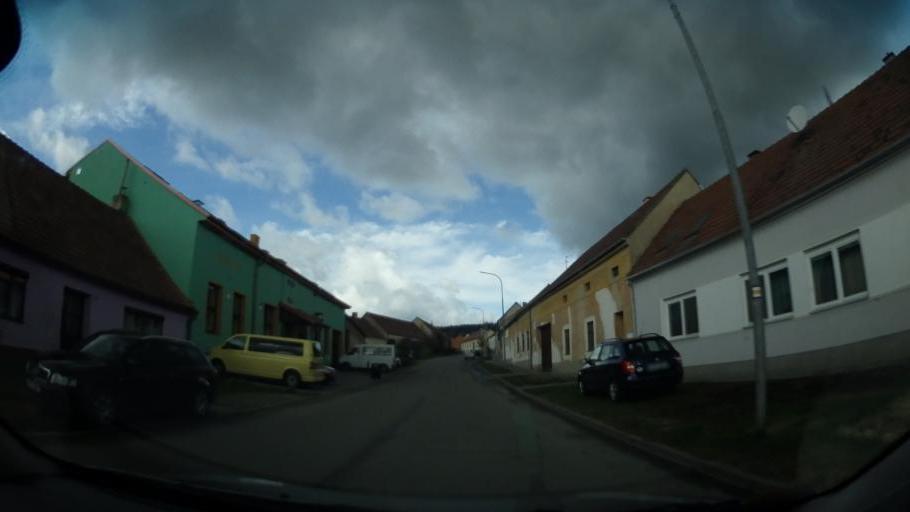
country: CZ
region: South Moravian
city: Ricany
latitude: 49.2367
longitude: 16.4040
